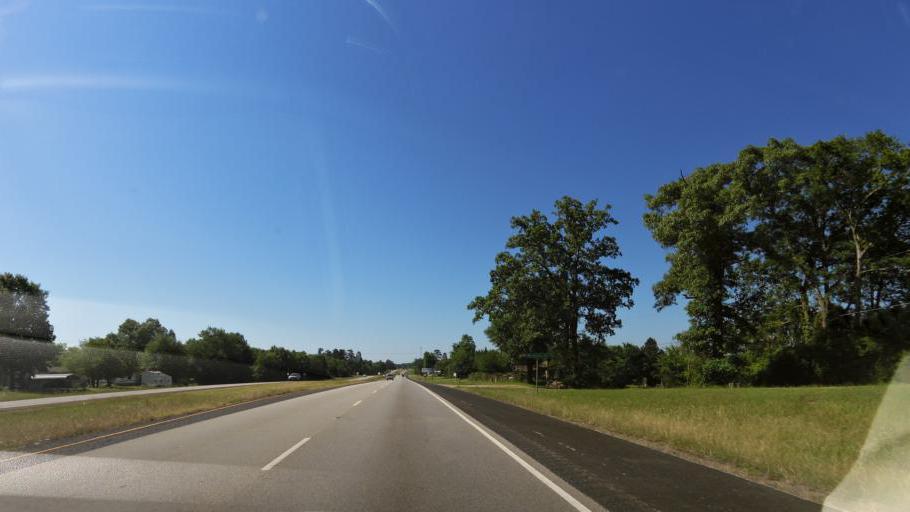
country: US
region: Texas
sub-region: Angelina County
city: Redland
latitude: 31.4439
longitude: -94.7267
